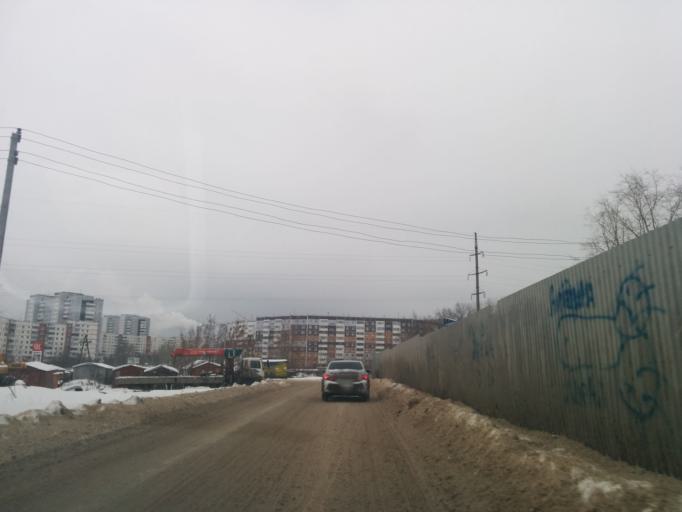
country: RU
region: Perm
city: Perm
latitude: 58.0142
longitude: 56.3042
